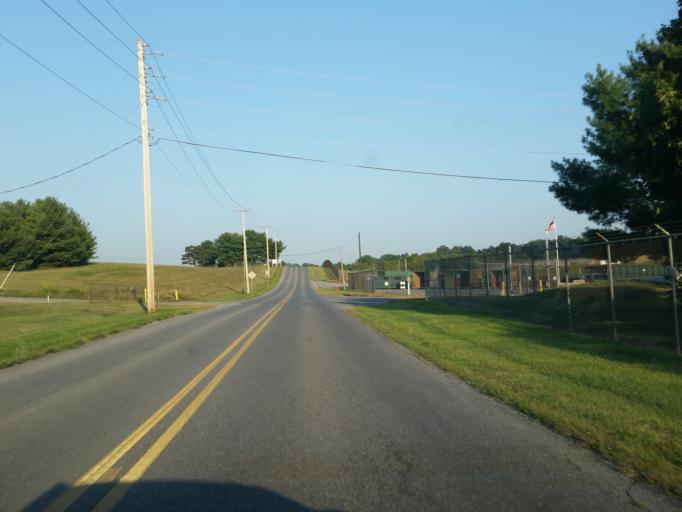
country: US
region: Pennsylvania
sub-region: Lebanon County
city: Cleona
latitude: 40.3709
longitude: -76.4912
